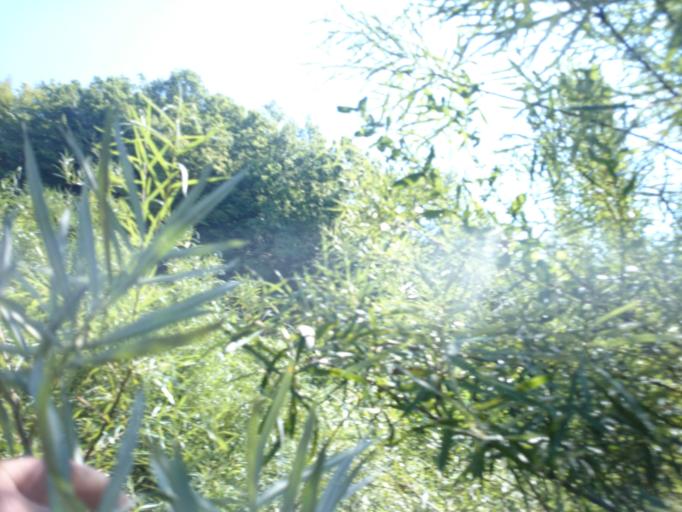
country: AL
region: Diber
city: Peshkopi
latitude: 41.6854
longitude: 20.4387
